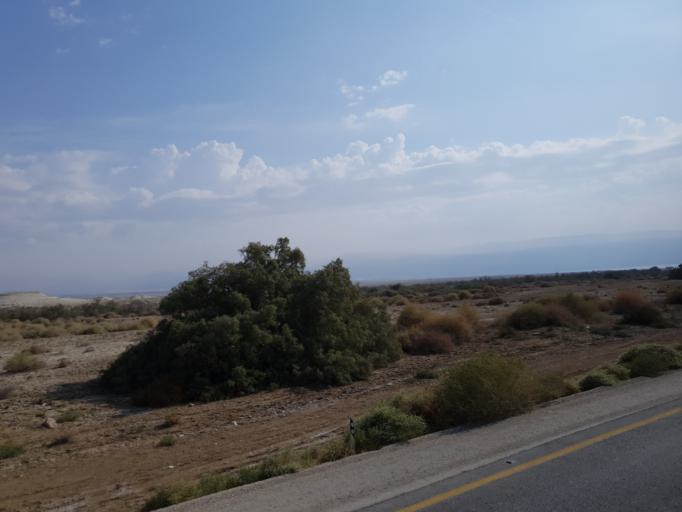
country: PS
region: West Bank
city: Jericho
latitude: 31.7868
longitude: 35.4998
